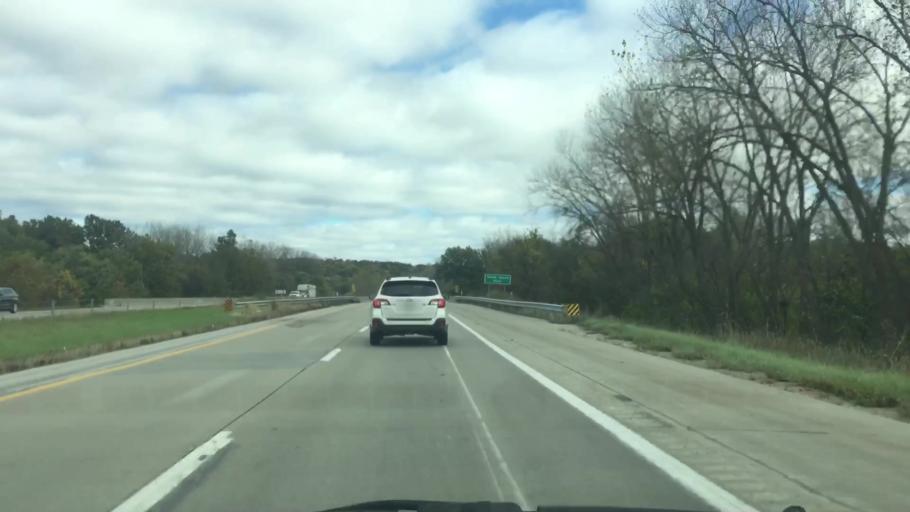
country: US
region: Iowa
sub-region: Jasper County
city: Colfax
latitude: 41.6831
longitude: -93.2948
